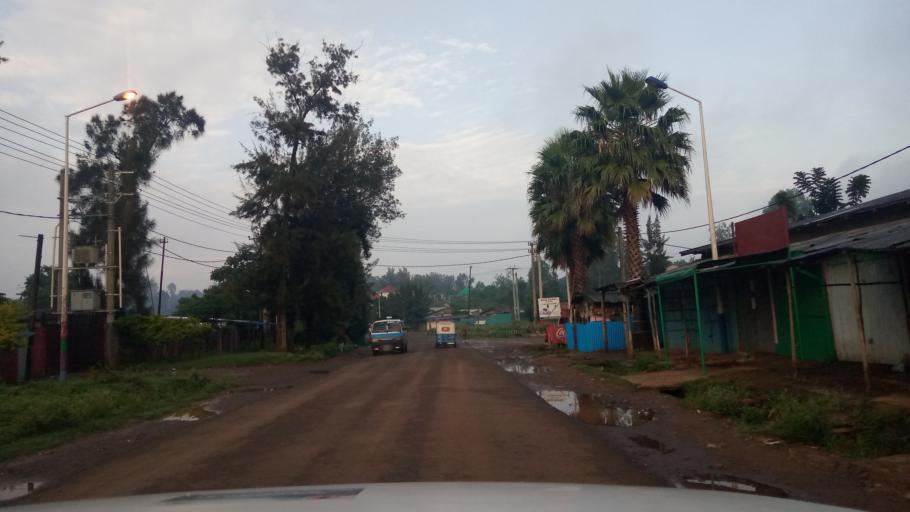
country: ET
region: Oromiya
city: Jima
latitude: 7.6816
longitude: 36.8413
